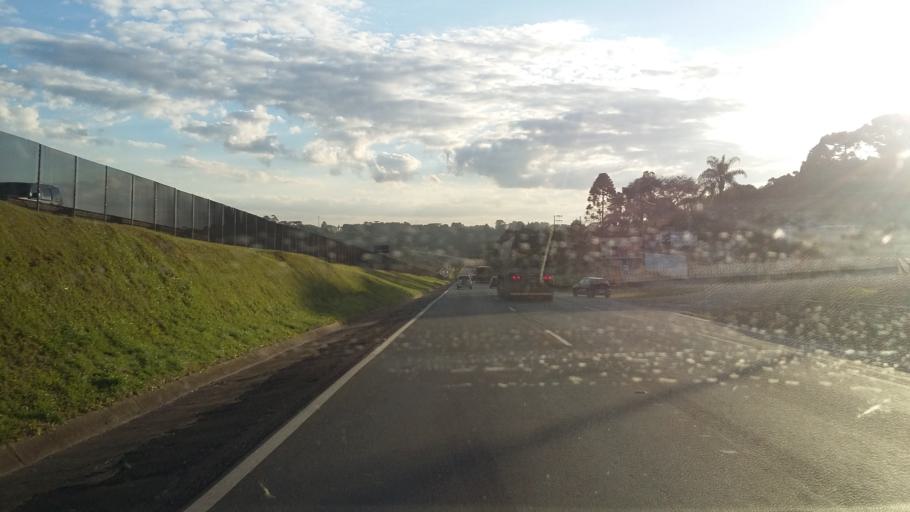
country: BR
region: Parana
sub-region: Campo Largo
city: Campo Largo
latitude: -25.4429
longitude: -49.4545
